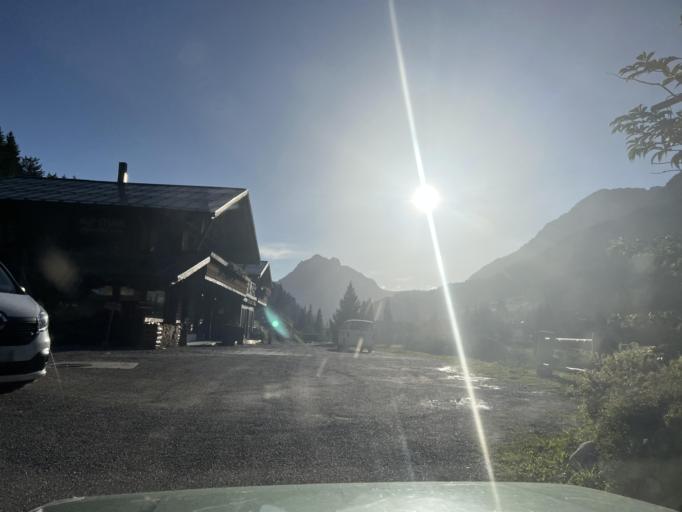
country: IT
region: Veneto
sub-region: Provincia di Belluno
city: Granvilla
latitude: 46.5702
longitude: 12.7175
